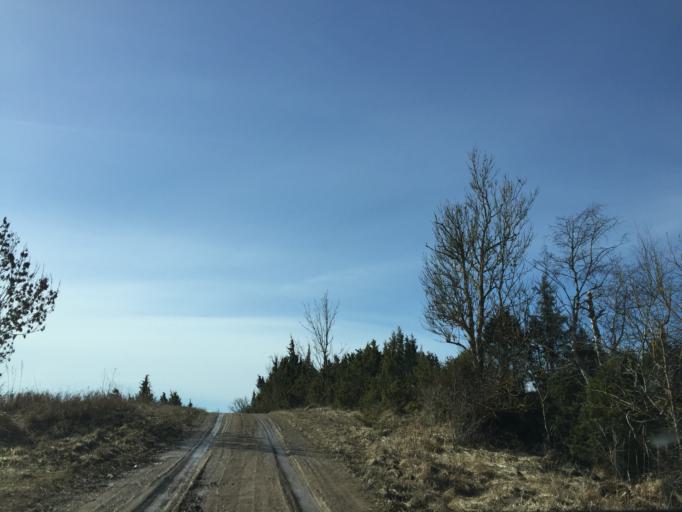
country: EE
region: Laeaene
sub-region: Haapsalu linn
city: Haapsalu
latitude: 58.6539
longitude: 23.5140
